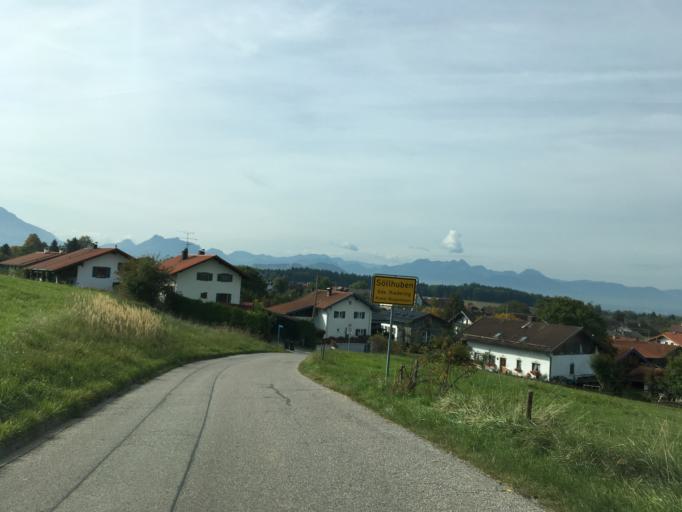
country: DE
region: Bavaria
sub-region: Upper Bavaria
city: Frasdorf
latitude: 47.8354
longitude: 12.2567
